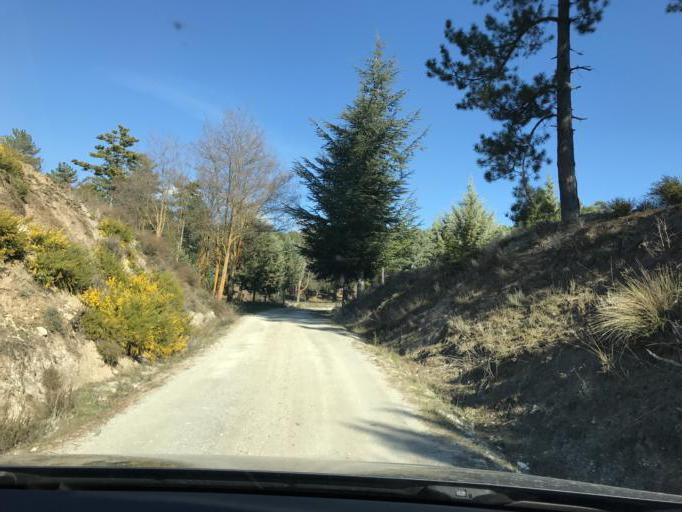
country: ES
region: Andalusia
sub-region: Provincia de Granada
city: Beas de Granada
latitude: 37.2347
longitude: -3.4411
